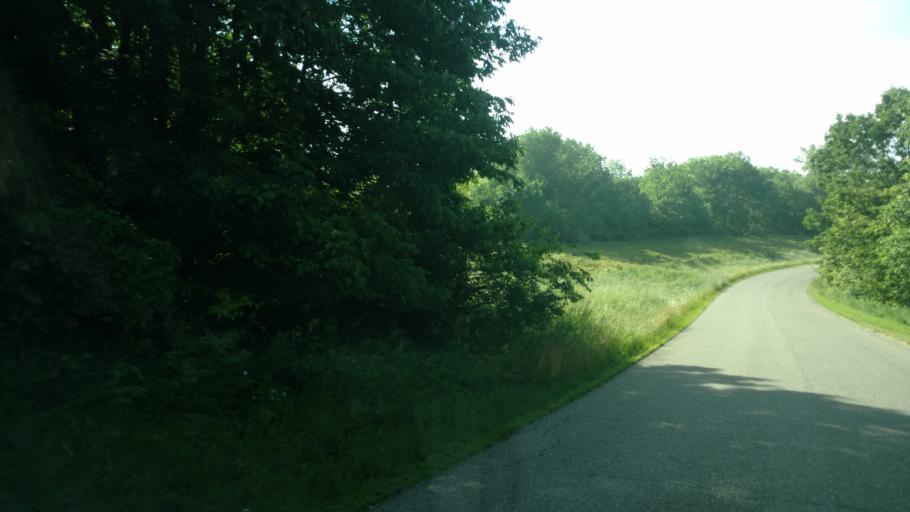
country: US
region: Wisconsin
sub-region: Vernon County
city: Hillsboro
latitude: 43.5907
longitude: -90.2162
